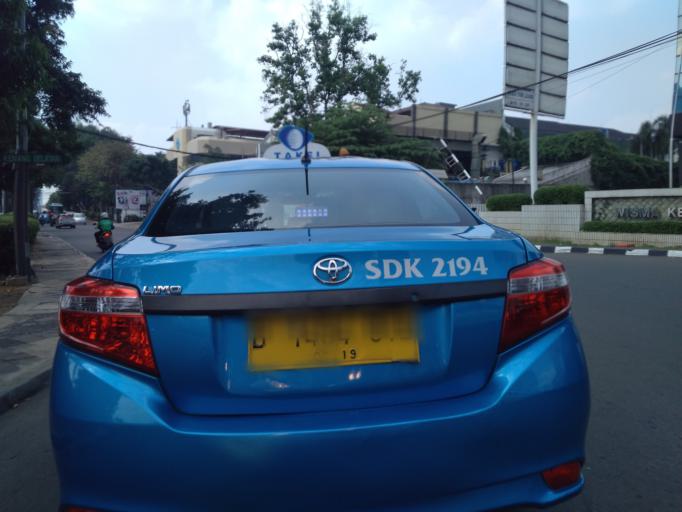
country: ID
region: Jakarta Raya
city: Jakarta
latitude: -6.2730
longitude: 106.8151
